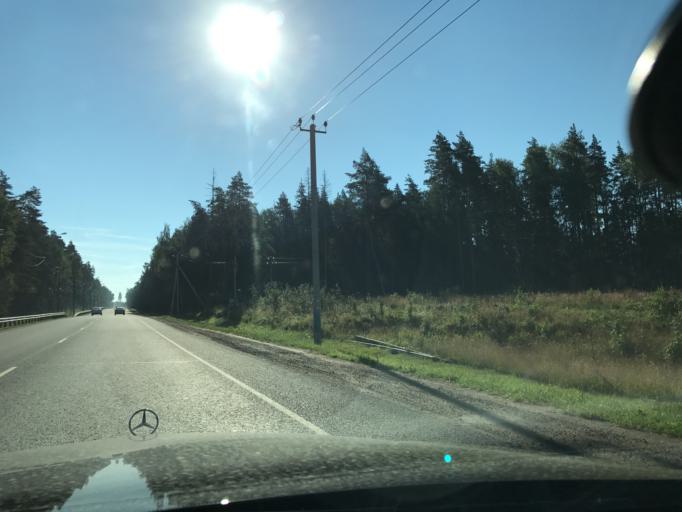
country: RU
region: Moskovskaya
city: Sverdlovskiy
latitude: 55.9280
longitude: 38.1813
